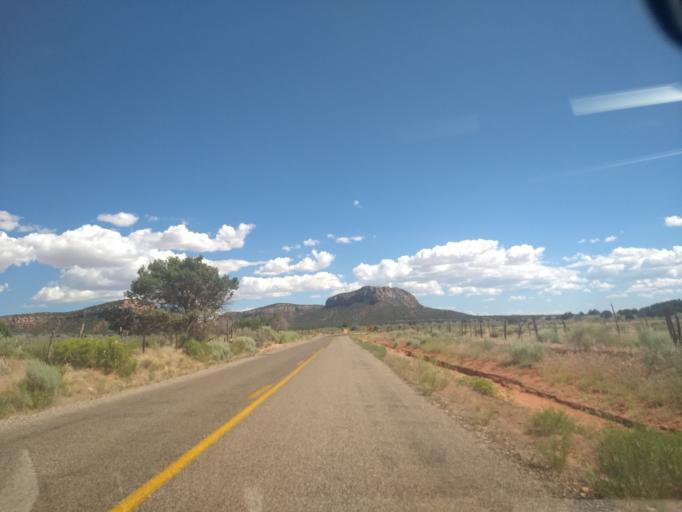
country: US
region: Utah
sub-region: Washington County
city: Hildale
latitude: 36.9485
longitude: -112.8746
